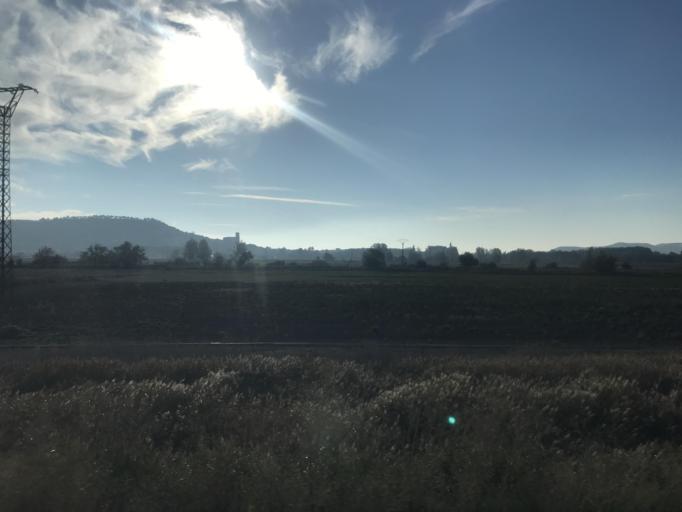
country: ES
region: Castille and Leon
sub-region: Provincia de Burgos
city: Villaquiran de los Infantes
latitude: 42.2127
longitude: -4.0039
